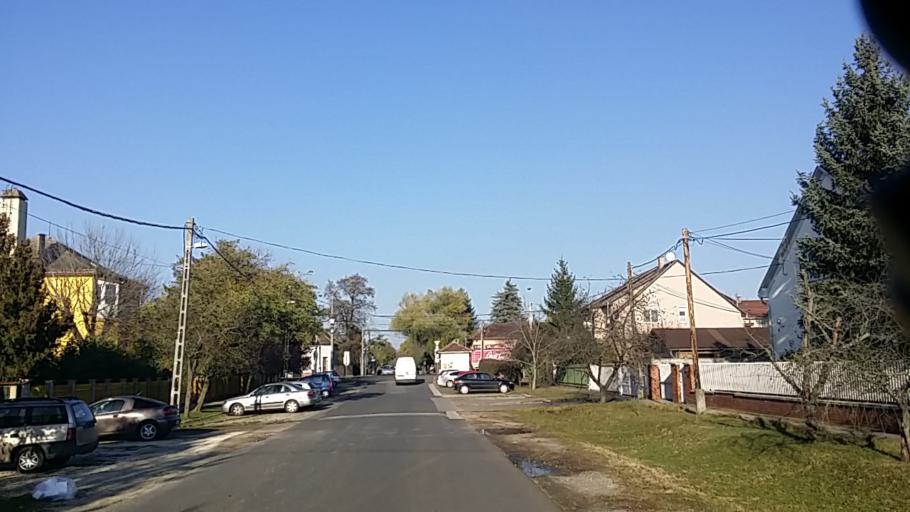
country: HU
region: Budapest
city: Budapest XVIII. keruelet
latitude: 47.4320
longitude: 19.2065
